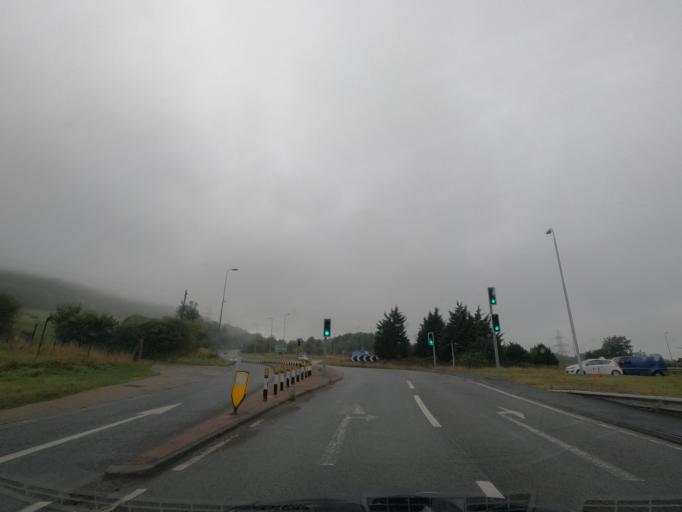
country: GB
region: England
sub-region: Redcar and Cleveland
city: South Bank
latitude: 54.5660
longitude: -1.1215
